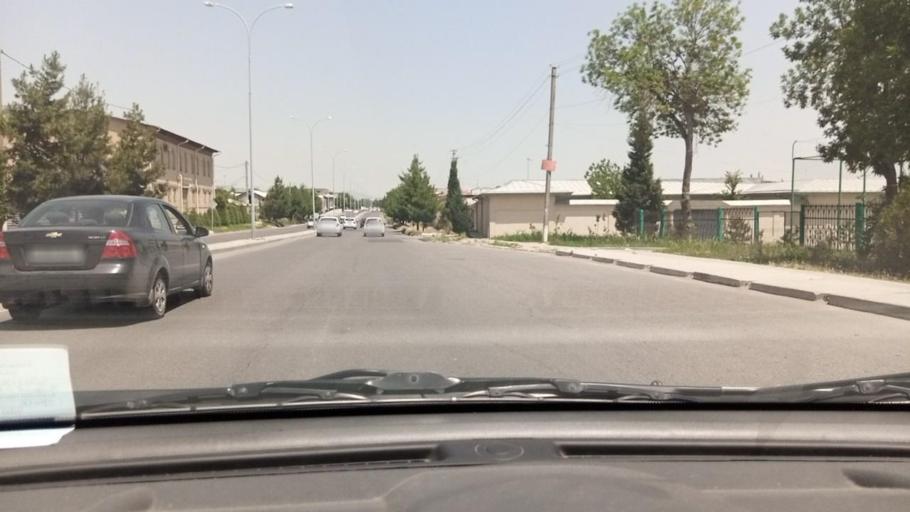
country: UZ
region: Toshkent Shahri
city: Tashkent
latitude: 41.2417
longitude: 69.1983
